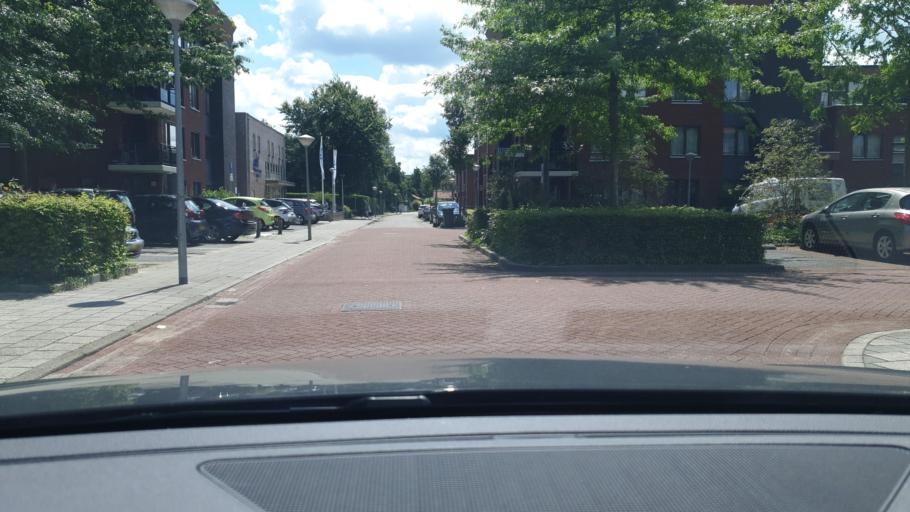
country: NL
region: North Brabant
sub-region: Gemeente Uden
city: Uden
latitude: 51.6602
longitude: 5.6088
